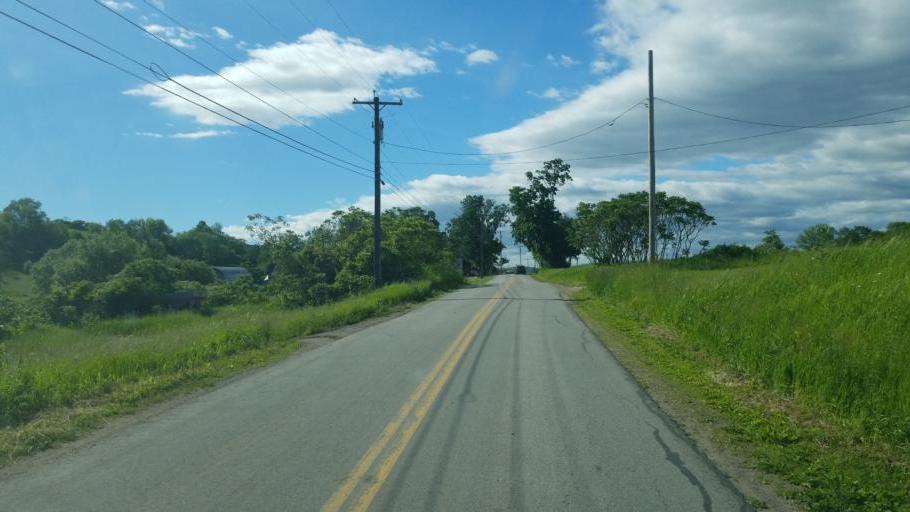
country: US
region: New York
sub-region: Montgomery County
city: Fort Plain
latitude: 42.9595
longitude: -74.6379
